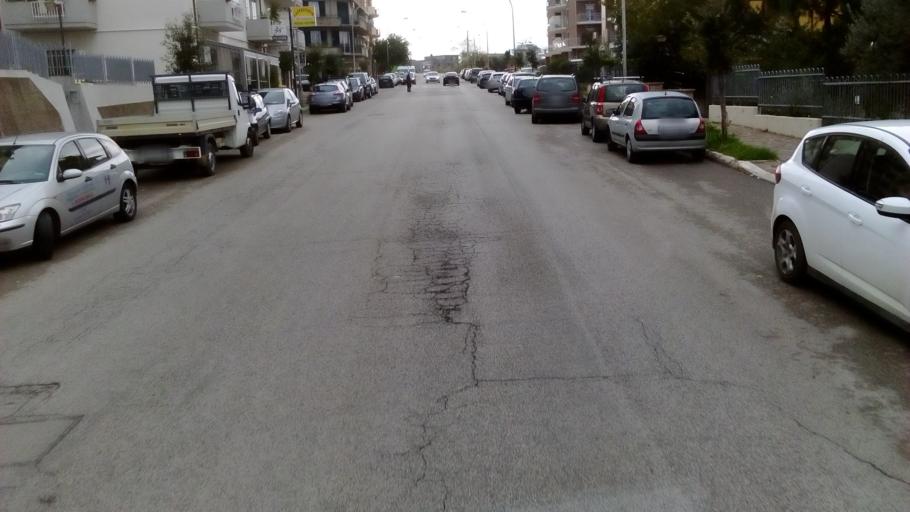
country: IT
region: Abruzzo
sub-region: Provincia di Chieti
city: Vasto
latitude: 42.1050
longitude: 14.7023
